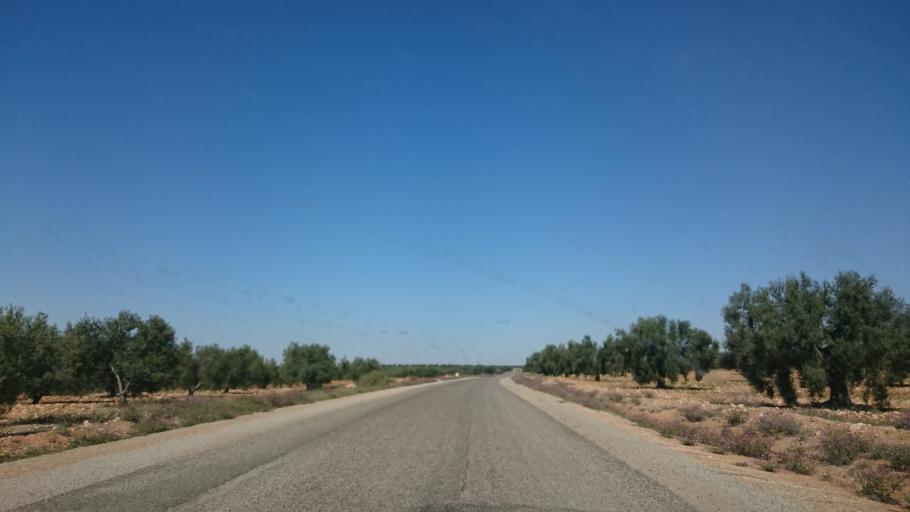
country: TN
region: Safaqis
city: Sfax
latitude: 34.8592
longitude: 10.4263
